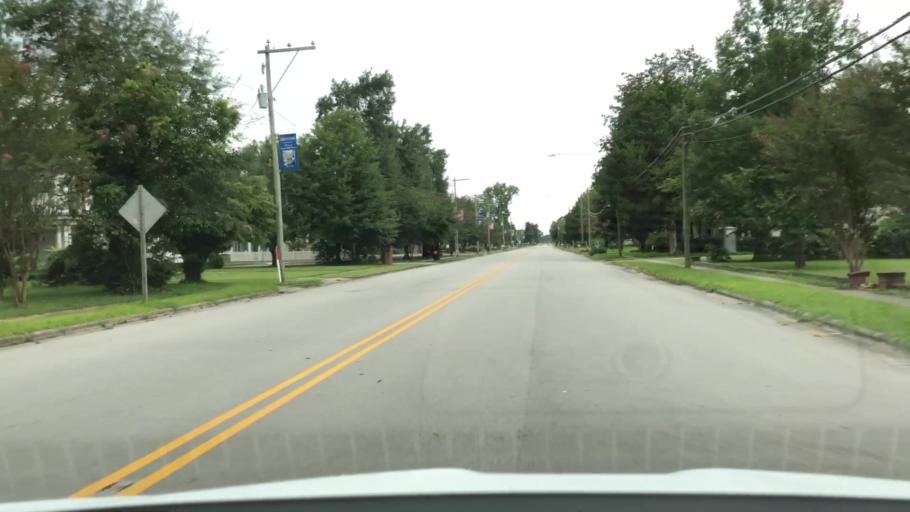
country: US
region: North Carolina
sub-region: Jones County
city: Trenton
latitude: 35.0647
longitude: -77.3567
